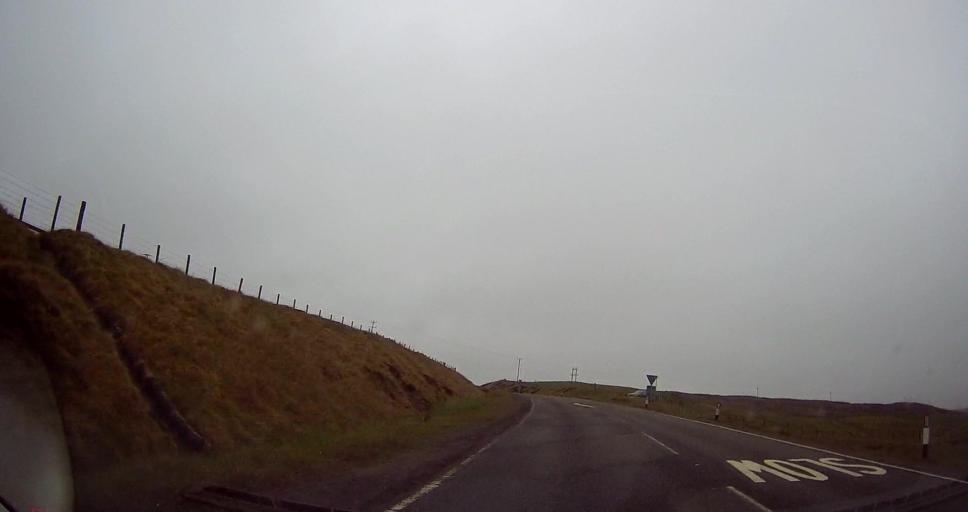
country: GB
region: Scotland
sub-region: Shetland Islands
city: Lerwick
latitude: 60.1375
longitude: -1.2151
